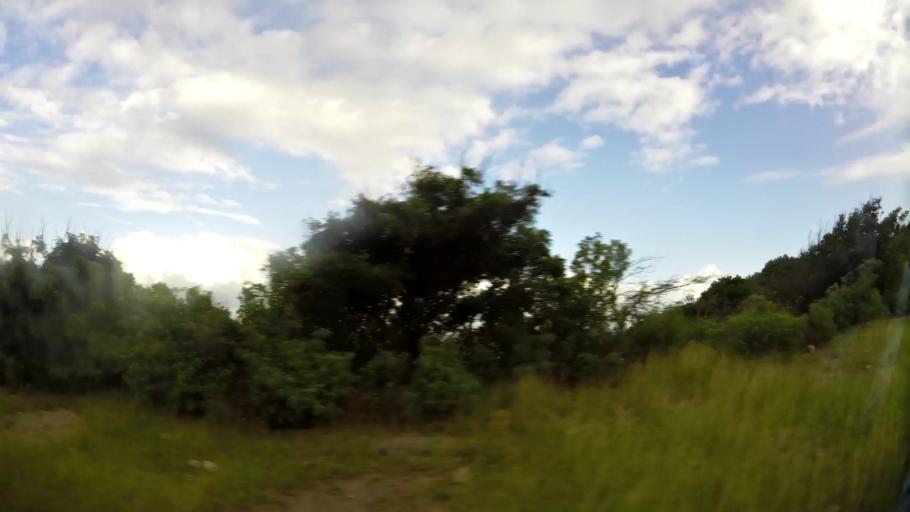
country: MS
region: Saint Peter
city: Brades
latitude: 16.7718
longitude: -62.1709
